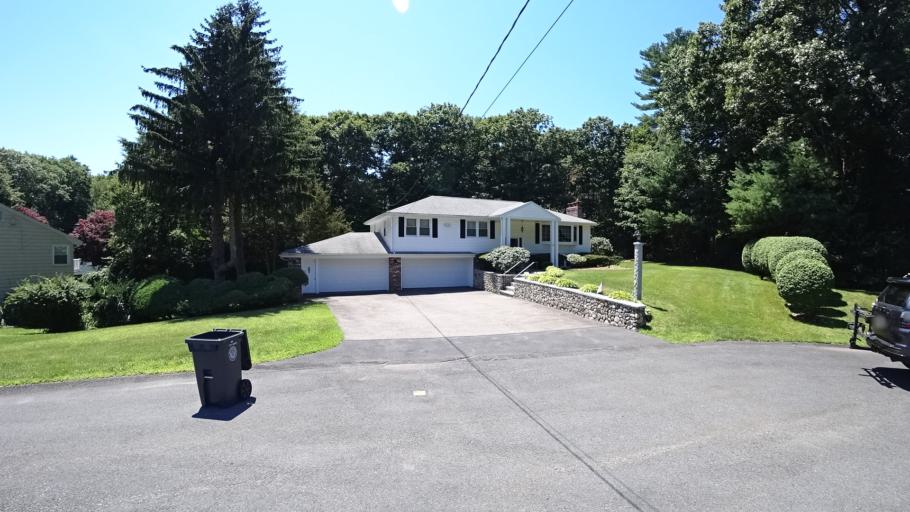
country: US
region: Massachusetts
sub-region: Norfolk County
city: Dedham
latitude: 42.2375
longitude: -71.1868
